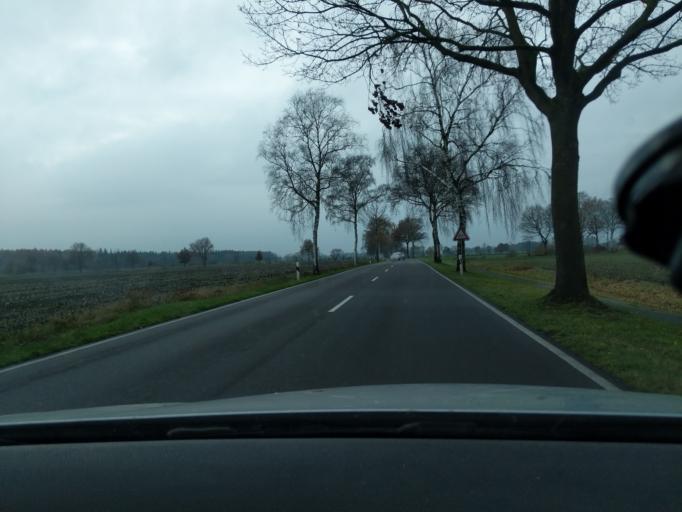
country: DE
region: Lower Saxony
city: Ahlerstedt
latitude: 53.3755
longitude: 9.4553
